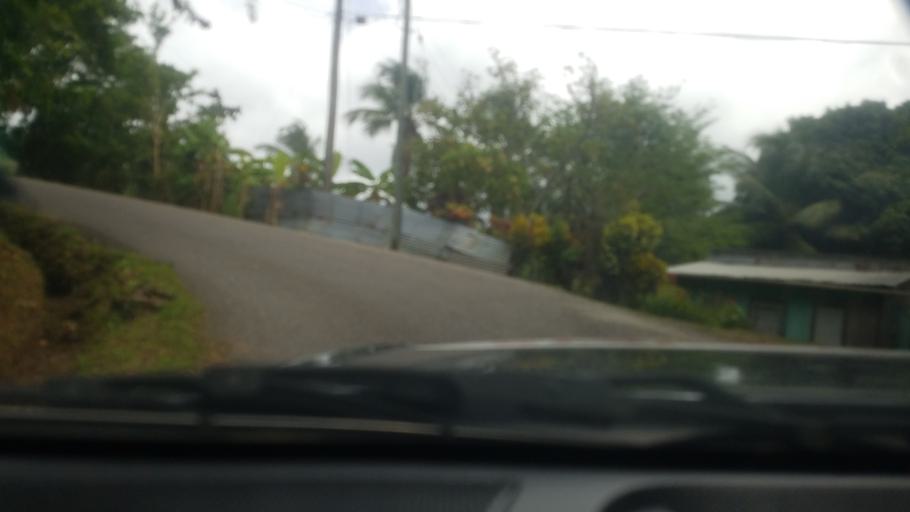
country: LC
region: Micoud Quarter
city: Micoud
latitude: 13.7974
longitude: -60.9505
